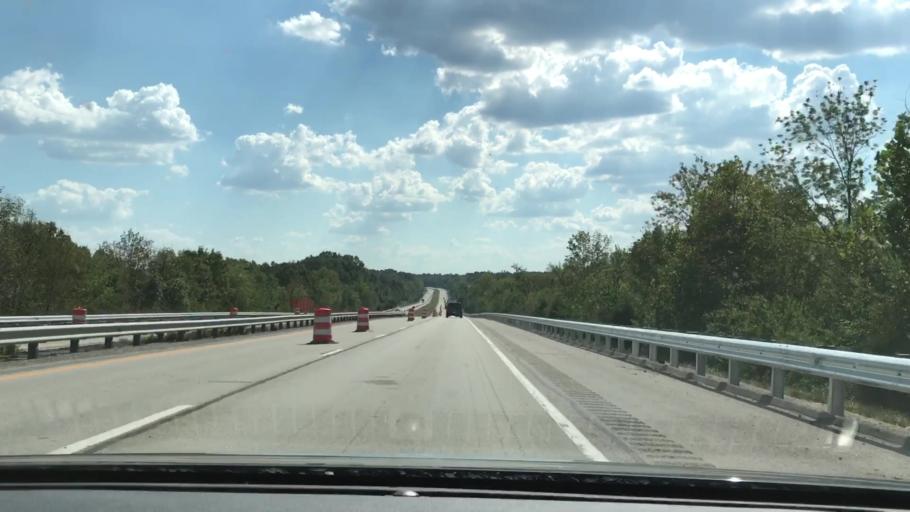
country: US
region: Kentucky
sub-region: Ohio County
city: Oak Grove
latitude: 37.2808
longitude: -86.7441
